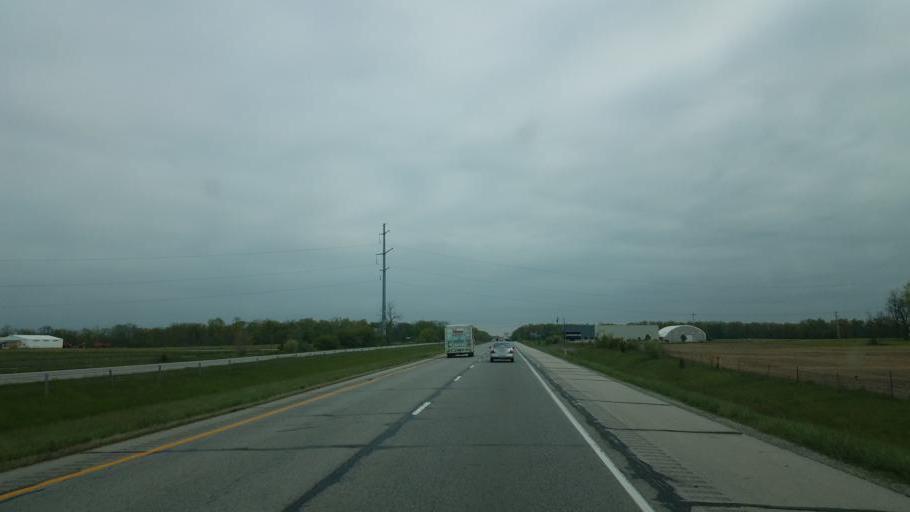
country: US
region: Indiana
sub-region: Allen County
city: Leo-Cedarville
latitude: 41.2630
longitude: -85.0866
